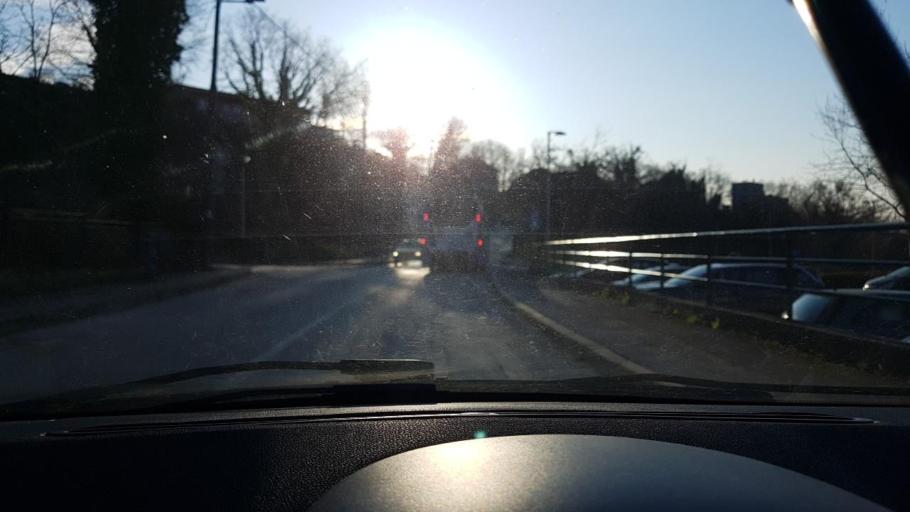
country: HR
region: Grad Zagreb
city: Zagreb
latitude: 45.8516
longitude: 15.9912
